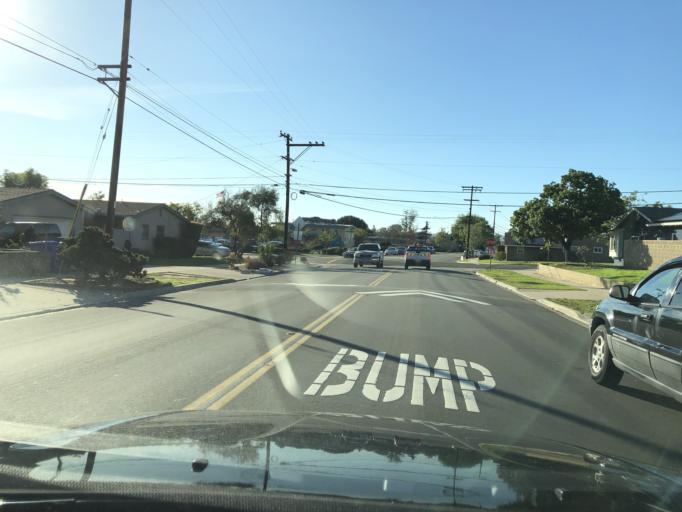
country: US
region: California
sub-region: San Diego County
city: La Jolla
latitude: 32.8209
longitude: -117.1856
